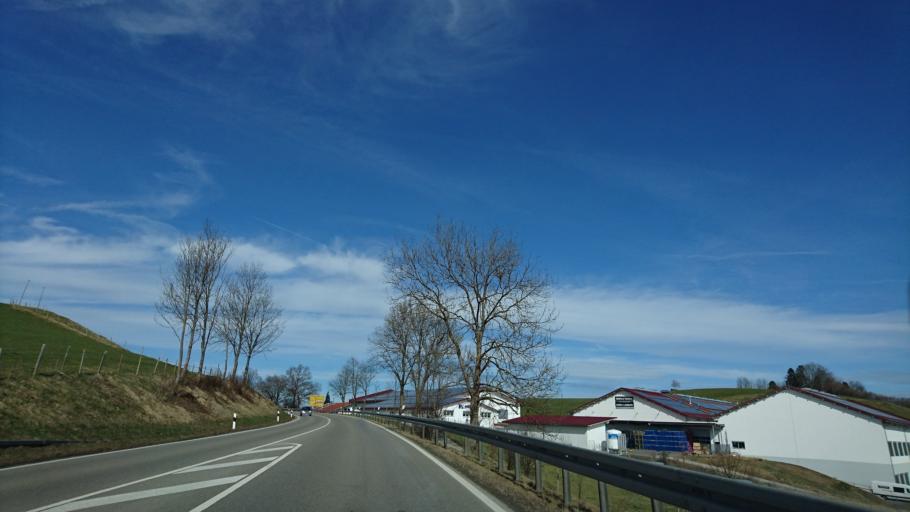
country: DE
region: Bavaria
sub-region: Swabia
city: Schwangau
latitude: 47.6098
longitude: 10.7126
